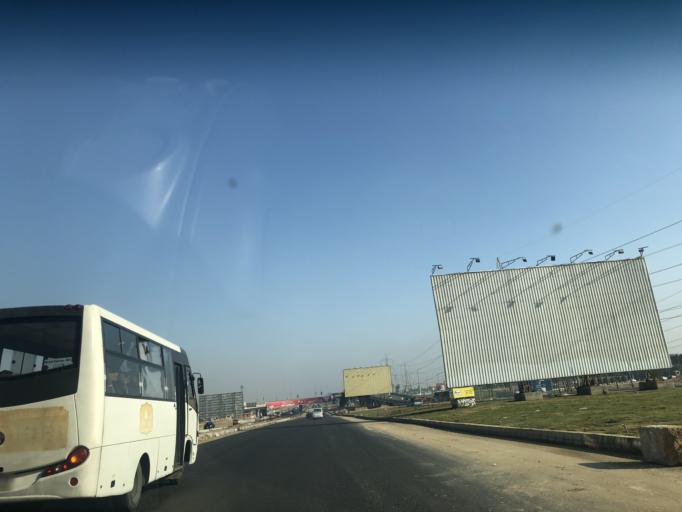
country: EG
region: Al Jizah
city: Madinat Sittah Uktubar
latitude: 29.9720
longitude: 31.0082
